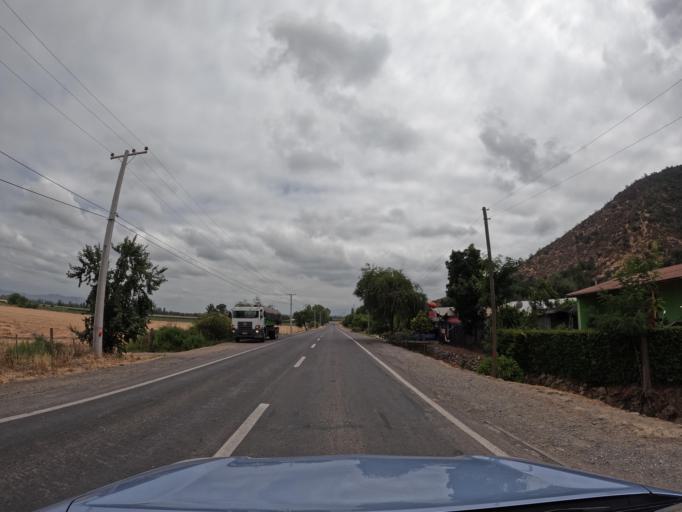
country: CL
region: Maule
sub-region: Provincia de Curico
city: Teno
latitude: -34.7785
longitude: -71.2307
